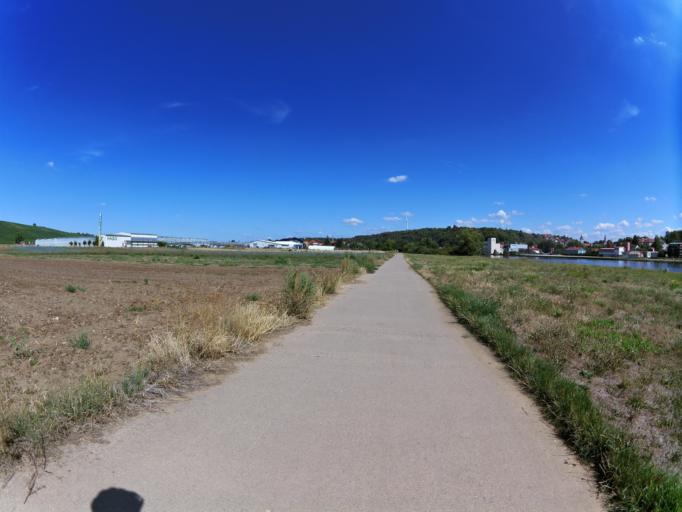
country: DE
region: Bavaria
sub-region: Regierungsbezirk Unterfranken
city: Segnitz
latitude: 49.6685
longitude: 10.1337
